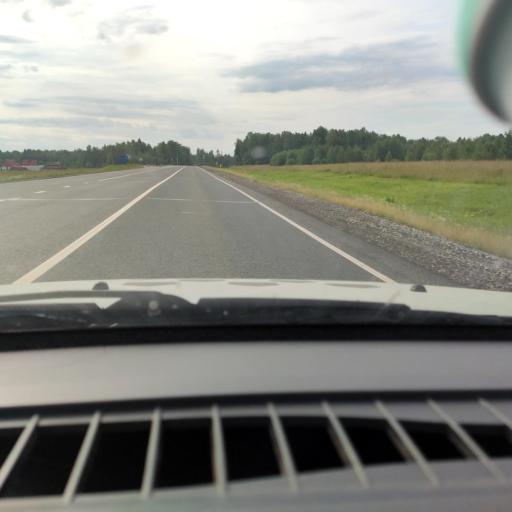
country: RU
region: Perm
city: Siva
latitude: 58.6296
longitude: 53.8650
